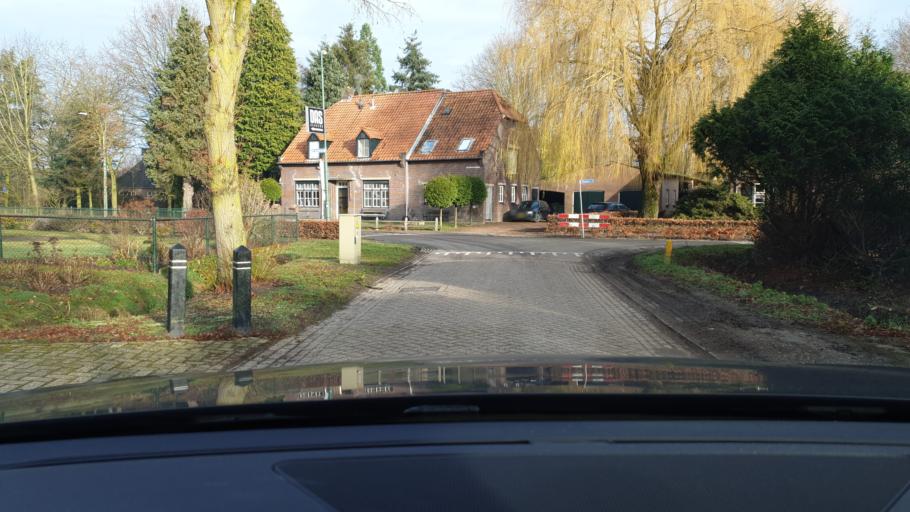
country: NL
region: North Brabant
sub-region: Gemeente Veldhoven
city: Oerle
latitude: 51.4418
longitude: 5.3438
